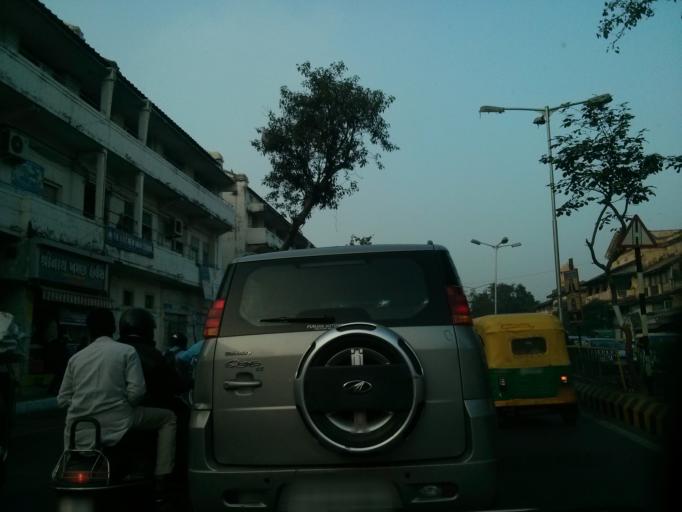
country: IN
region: Gujarat
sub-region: Ahmadabad
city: Ahmedabad
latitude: 23.0398
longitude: 72.5884
